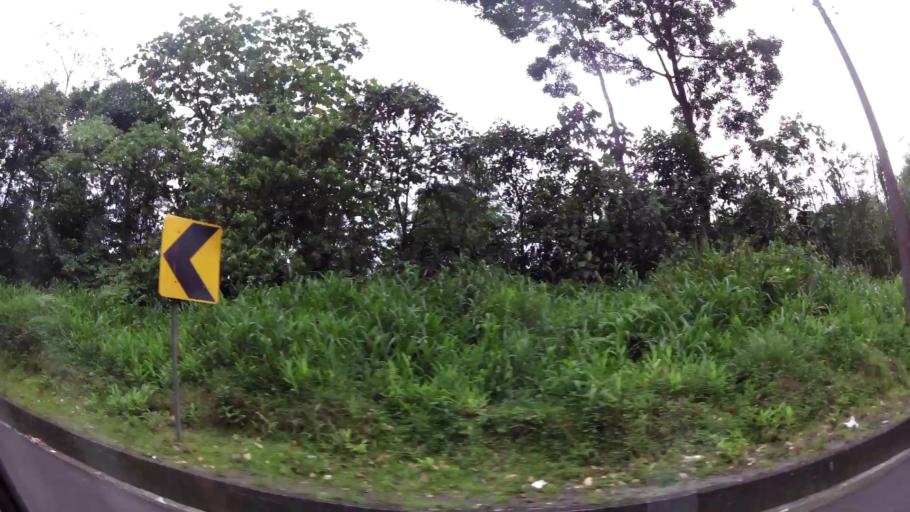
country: EC
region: Pastaza
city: Puyo
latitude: -1.5073
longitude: -78.0472
